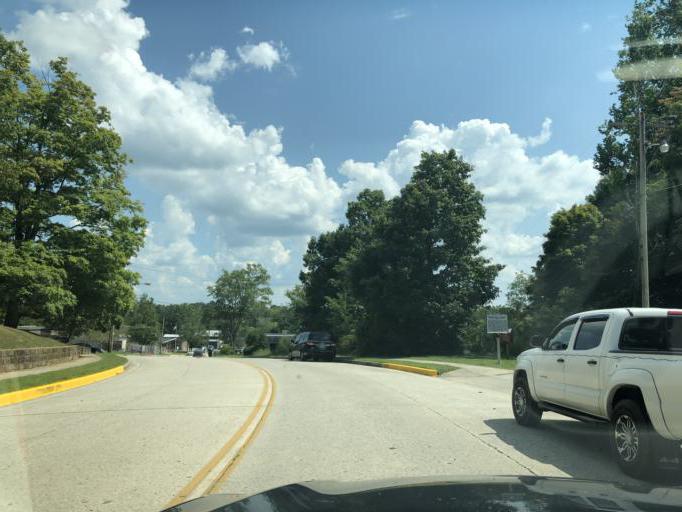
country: US
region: Tennessee
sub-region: Franklin County
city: Sewanee
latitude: 35.1974
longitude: -85.9193
